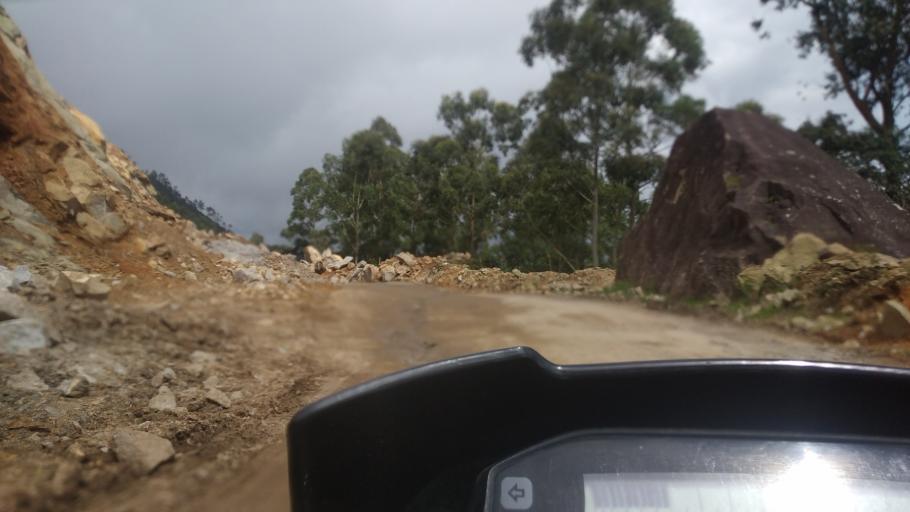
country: IN
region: Kerala
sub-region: Idukki
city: Munnar
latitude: 10.0369
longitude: 77.1276
